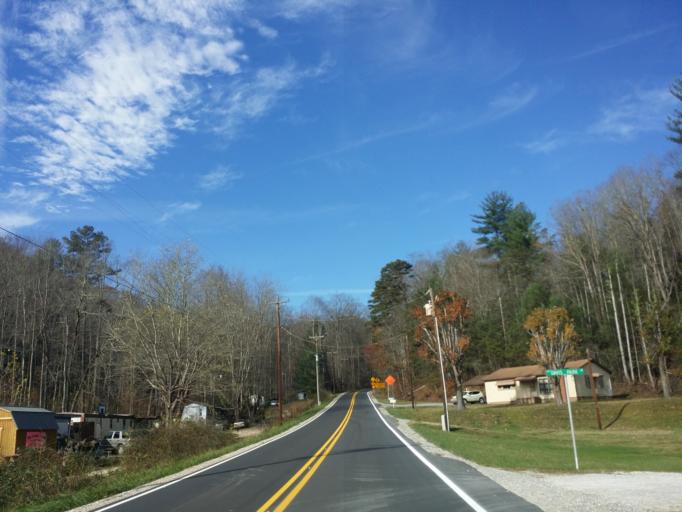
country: US
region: North Carolina
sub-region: McDowell County
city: Marion
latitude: 35.7172
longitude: -82.0743
